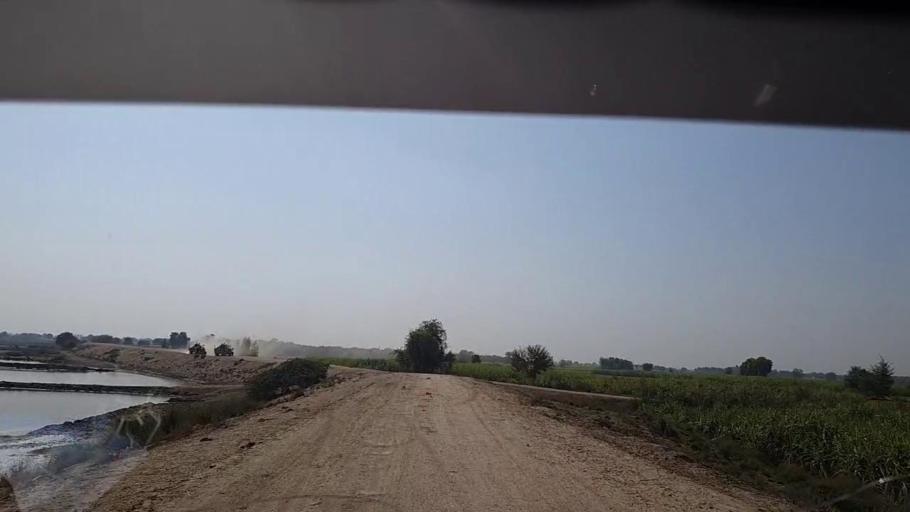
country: PK
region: Sindh
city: Naudero
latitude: 27.6578
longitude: 68.3766
